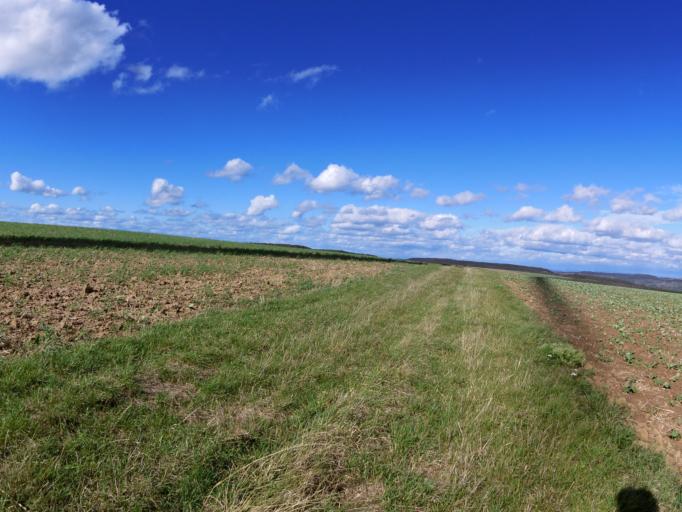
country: DE
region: Bavaria
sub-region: Regierungsbezirk Unterfranken
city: Erlabrunn
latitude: 49.8329
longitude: 9.8344
